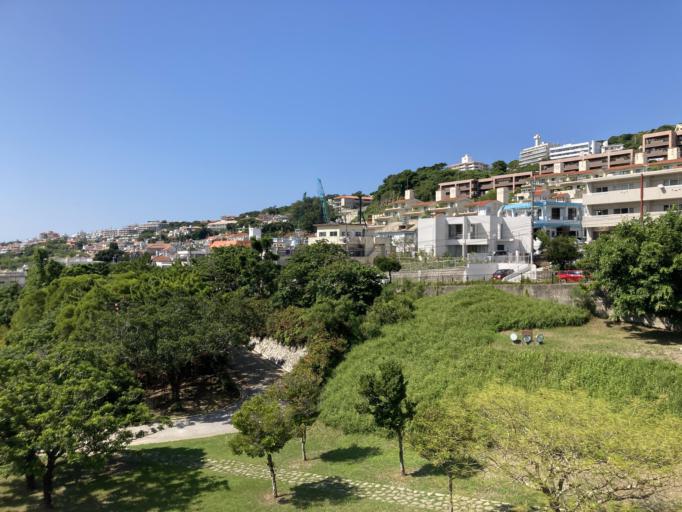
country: JP
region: Okinawa
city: Naha-shi
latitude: 26.2124
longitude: 127.7178
